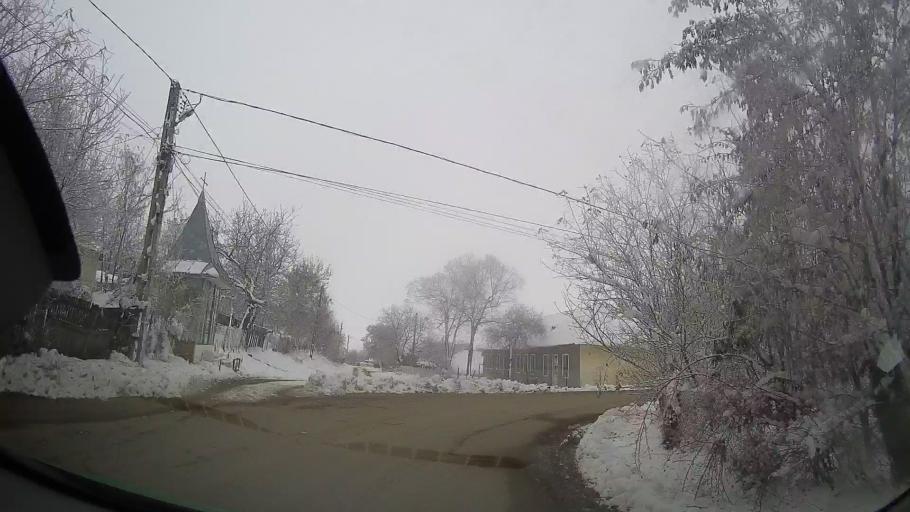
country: RO
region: Iasi
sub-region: Comuna Tansa
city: Suhulet
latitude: 46.8943
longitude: 27.2804
